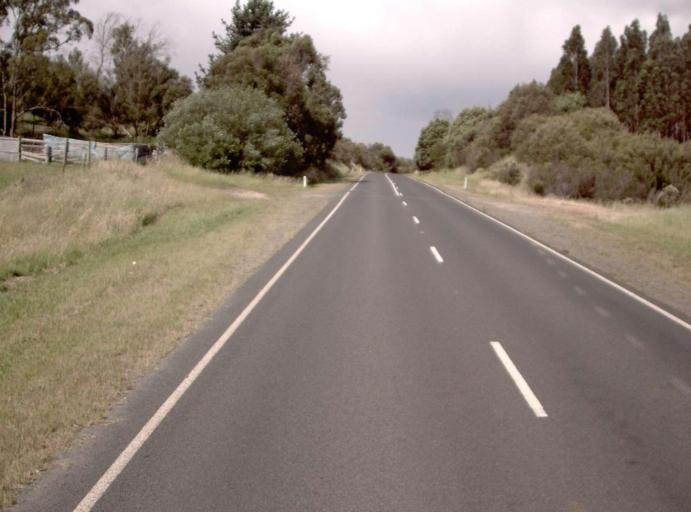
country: AU
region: Victoria
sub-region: Latrobe
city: Morwell
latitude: -38.1587
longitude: 146.4192
